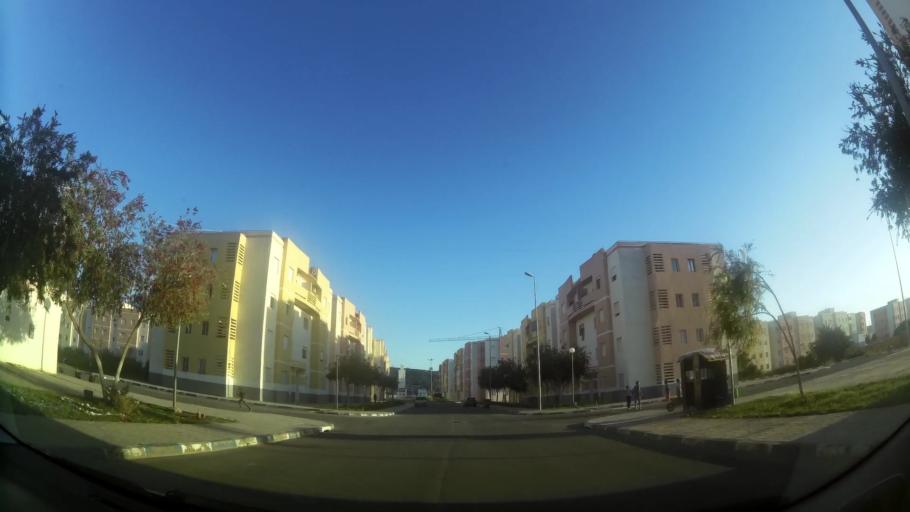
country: MA
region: Oriental
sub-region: Berkane-Taourirt
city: Madagh
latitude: 35.0777
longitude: -2.2374
